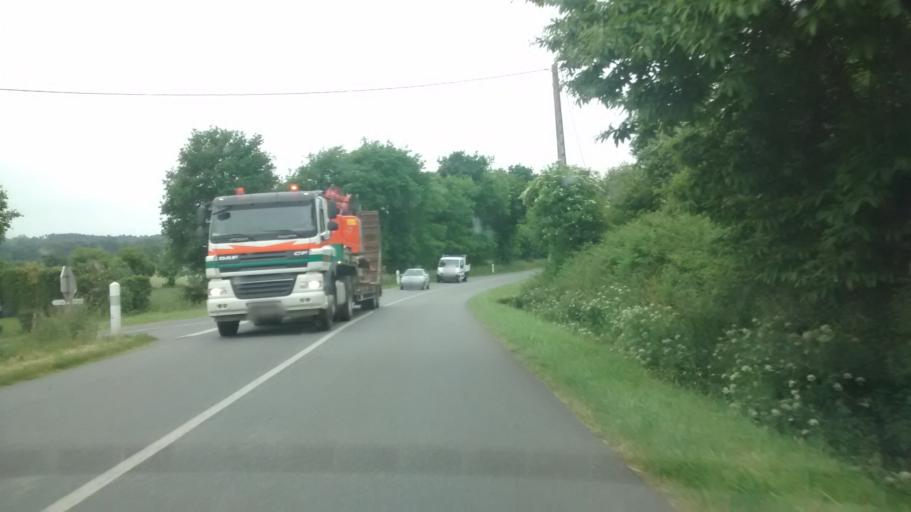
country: FR
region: Brittany
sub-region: Departement du Morbihan
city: Malestroit
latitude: 47.7938
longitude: -2.4196
